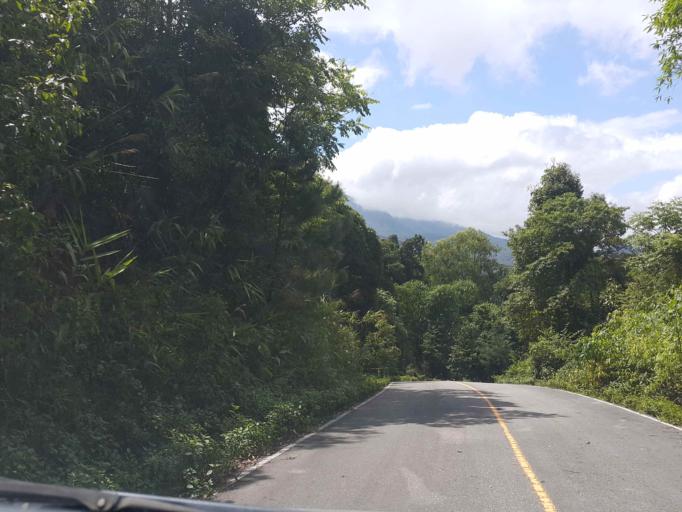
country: TH
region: Chiang Mai
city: Mae Chaem
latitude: 18.5148
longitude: 98.5295
